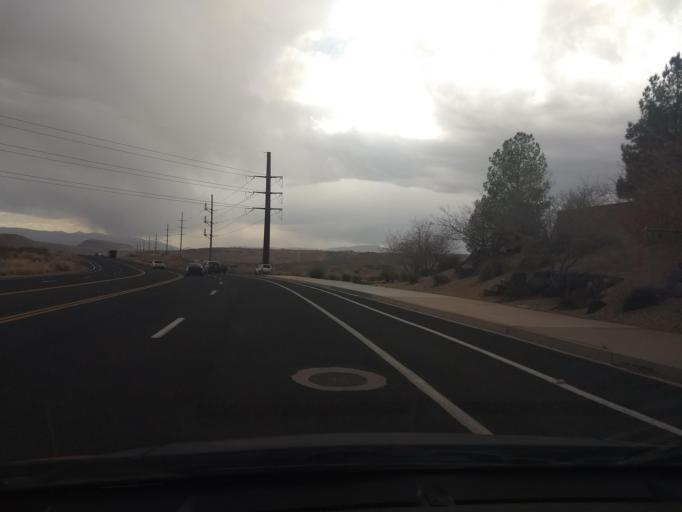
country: US
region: Utah
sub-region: Washington County
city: Washington
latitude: 37.1559
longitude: -113.4415
